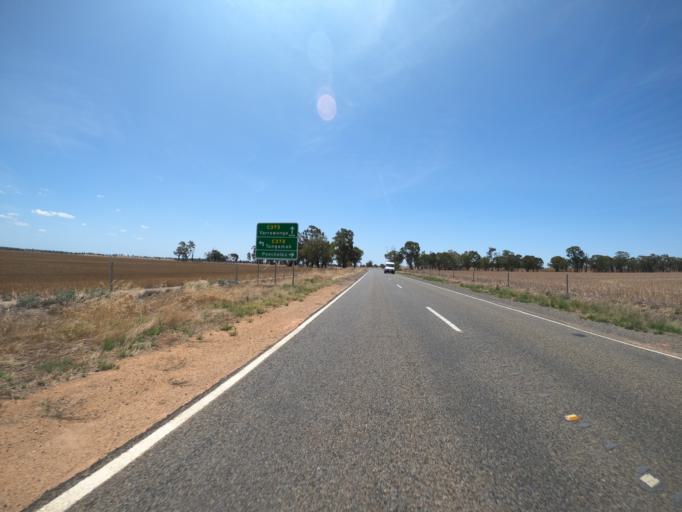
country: AU
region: Victoria
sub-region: Moira
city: Yarrawonga
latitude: -36.1592
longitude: 145.9672
